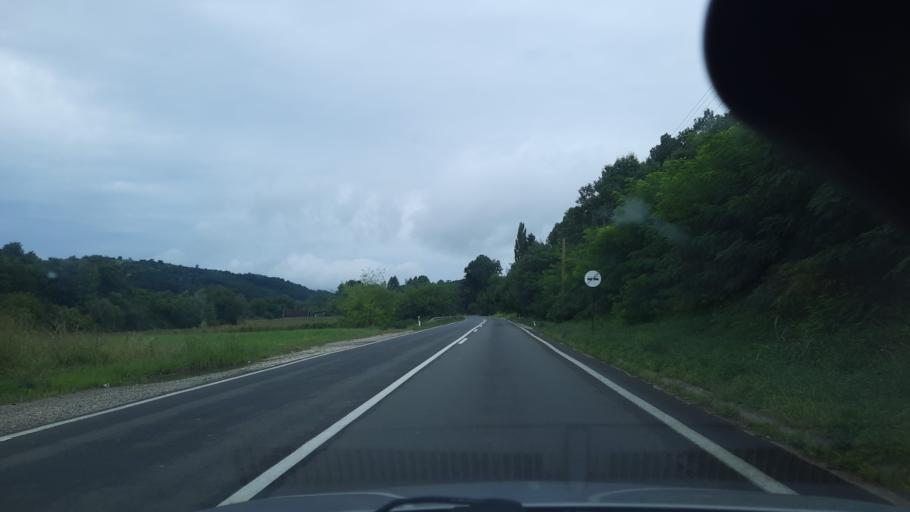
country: RS
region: Central Serbia
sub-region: Sumadijski Okrug
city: Knic
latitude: 43.9709
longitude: 20.8117
